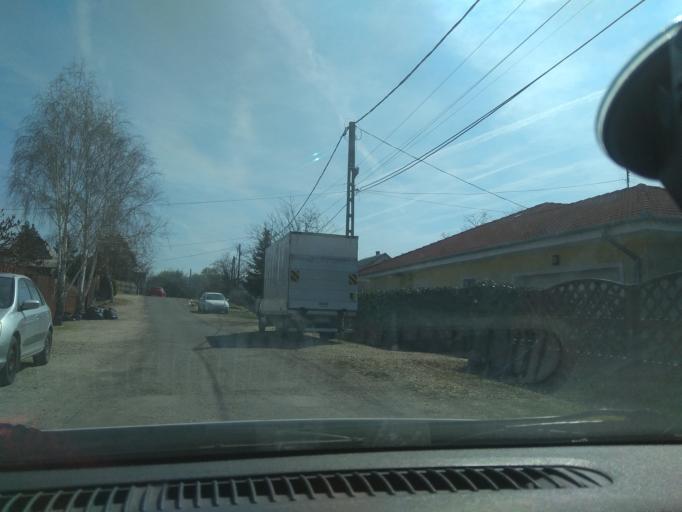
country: HU
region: Pest
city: Szigetszentmiklos
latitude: 47.3257
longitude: 19.0379
